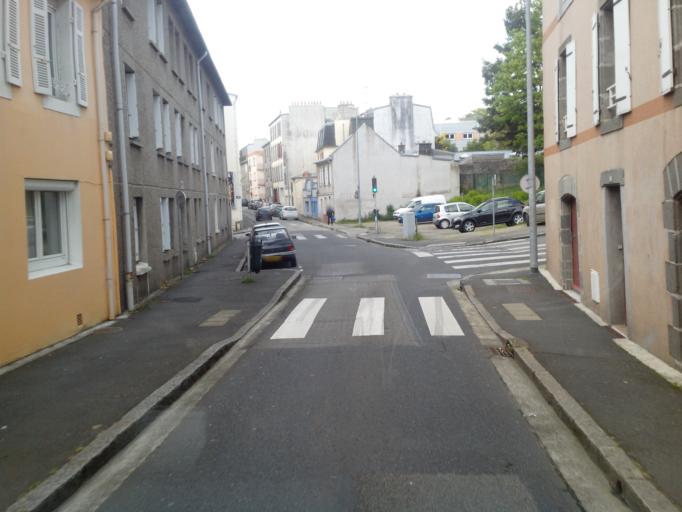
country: FR
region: Brittany
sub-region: Departement du Finistere
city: Brest
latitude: 48.3992
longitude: -4.4810
